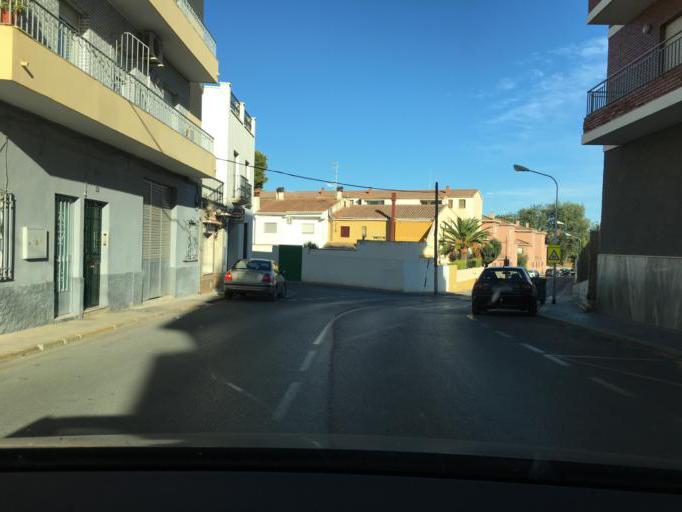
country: ES
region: Andalusia
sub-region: Provincia de Granada
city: Guadix
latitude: 37.2971
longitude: -3.1333
